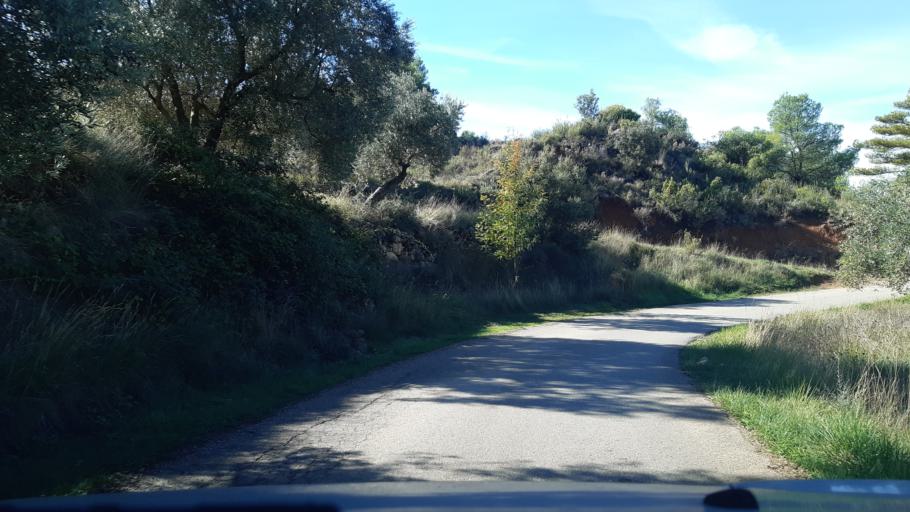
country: ES
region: Aragon
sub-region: Provincia de Teruel
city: Valderrobres
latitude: 40.8376
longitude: 0.2002
